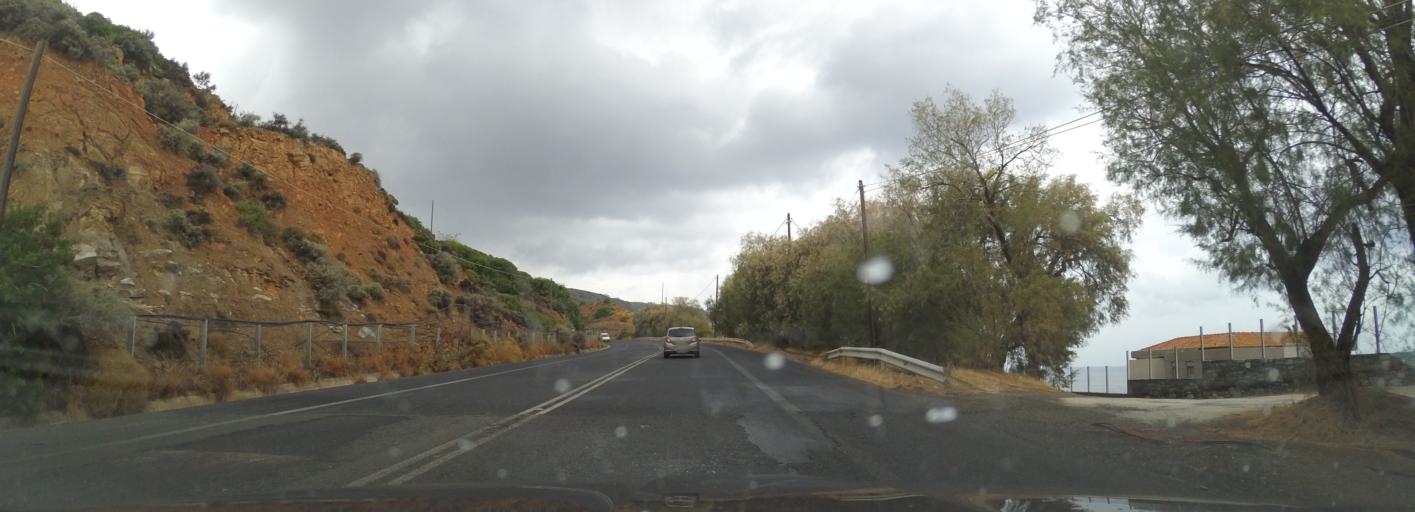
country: GR
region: Crete
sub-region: Nomos Irakleiou
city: Gazi
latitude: 35.3696
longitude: 25.0380
